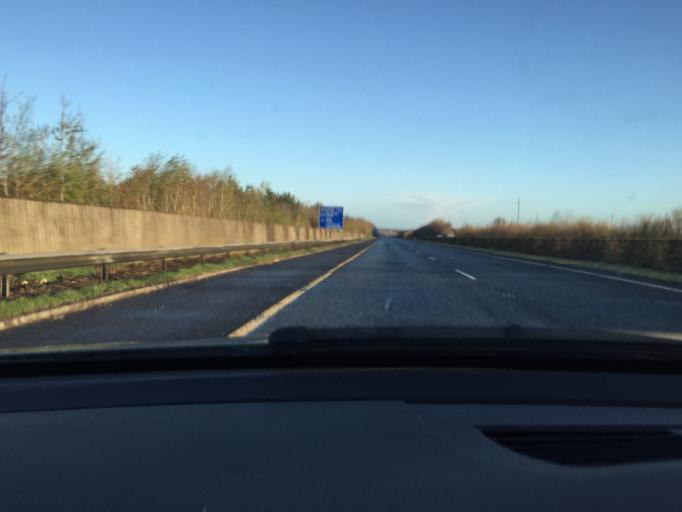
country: IE
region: Leinster
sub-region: Lu
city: Dunleer
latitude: 53.8388
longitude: -6.4165
